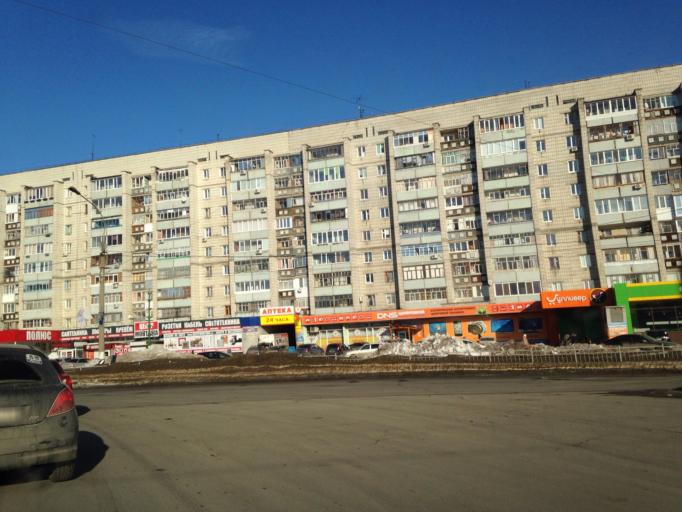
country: RU
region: Ulyanovsk
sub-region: Ulyanovskiy Rayon
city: Ulyanovsk
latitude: 54.3063
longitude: 48.3506
